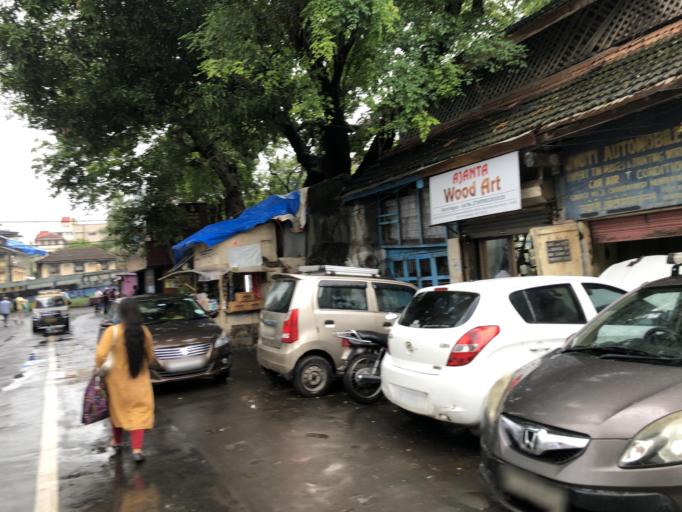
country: IN
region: Maharashtra
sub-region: Raigarh
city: Uran
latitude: 18.9454
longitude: 72.8252
